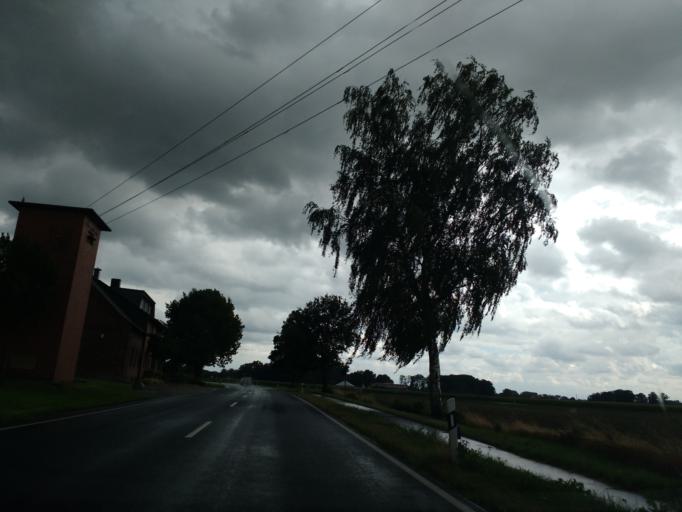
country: DE
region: Lower Saxony
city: Glandorf
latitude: 52.0907
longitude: 7.9708
